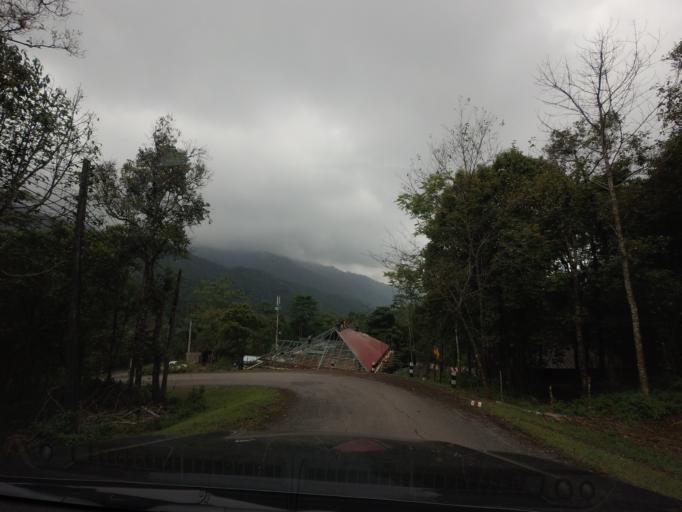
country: TH
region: Nan
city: Bo Kluea
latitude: 19.2029
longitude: 101.0812
